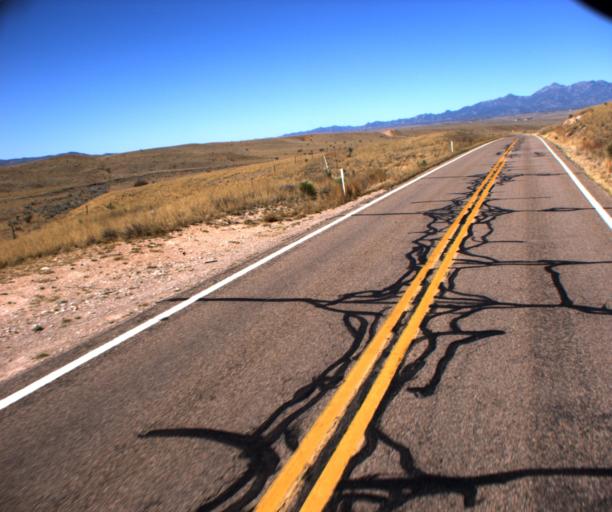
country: US
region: Arizona
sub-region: Cochise County
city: Huachuca City
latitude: 31.7108
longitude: -110.5667
